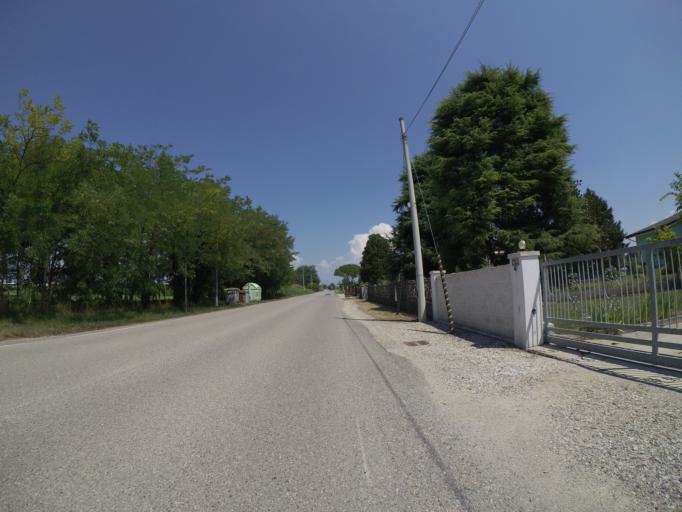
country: IT
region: Friuli Venezia Giulia
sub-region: Provincia di Udine
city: Mortegliano
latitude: 45.9265
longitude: 13.1512
